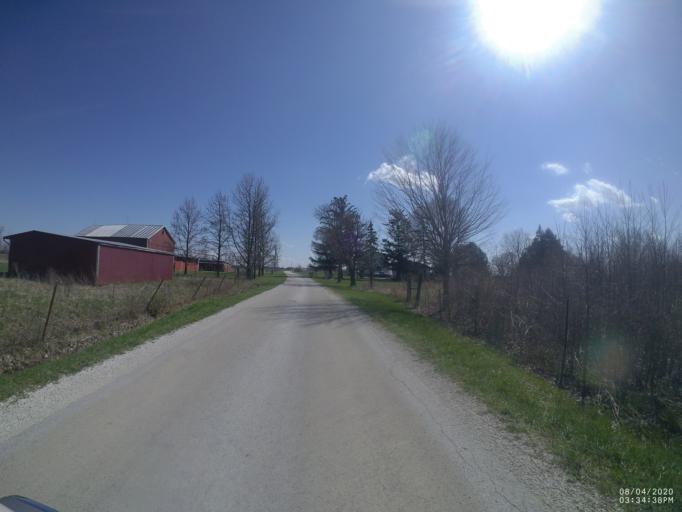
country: US
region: Ohio
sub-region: Sandusky County
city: Stony Prairie
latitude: 41.2624
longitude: -83.2574
